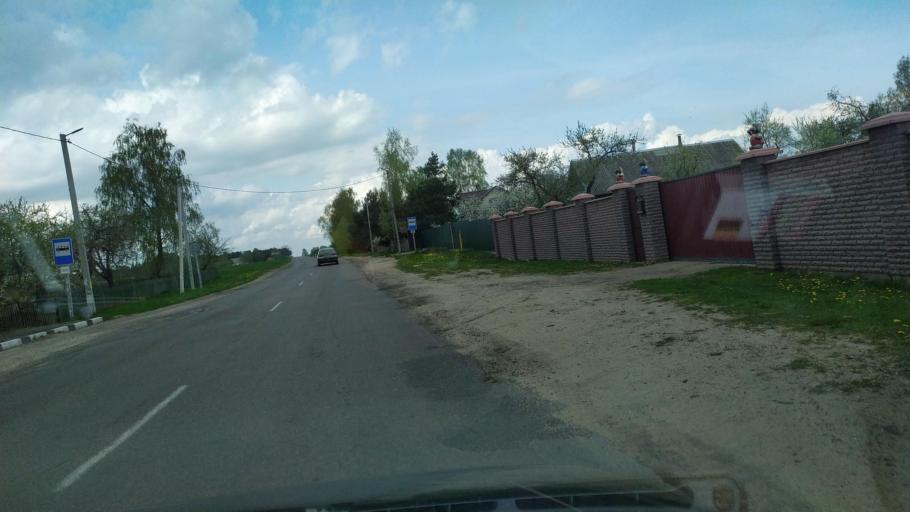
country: BY
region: Brest
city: Pruzhany
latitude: 52.5919
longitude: 24.4082
